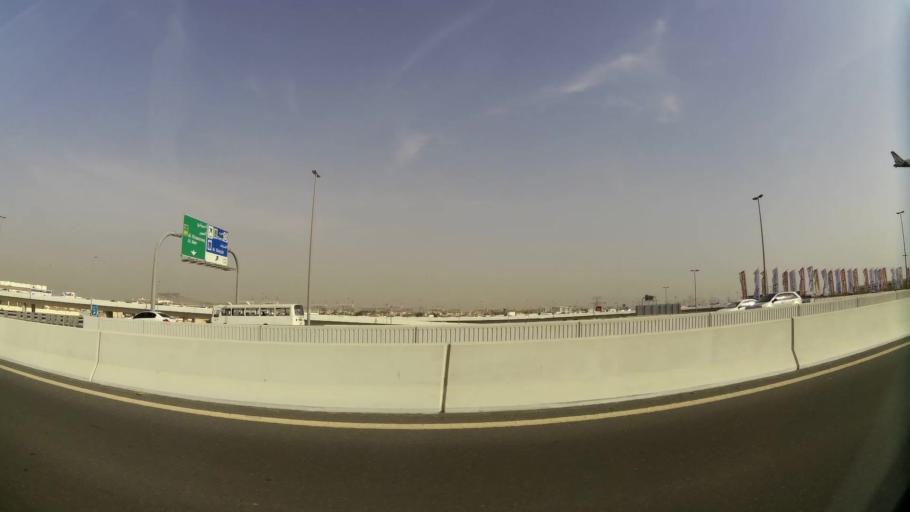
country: AE
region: Ash Shariqah
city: Sharjah
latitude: 25.2332
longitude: 55.4038
